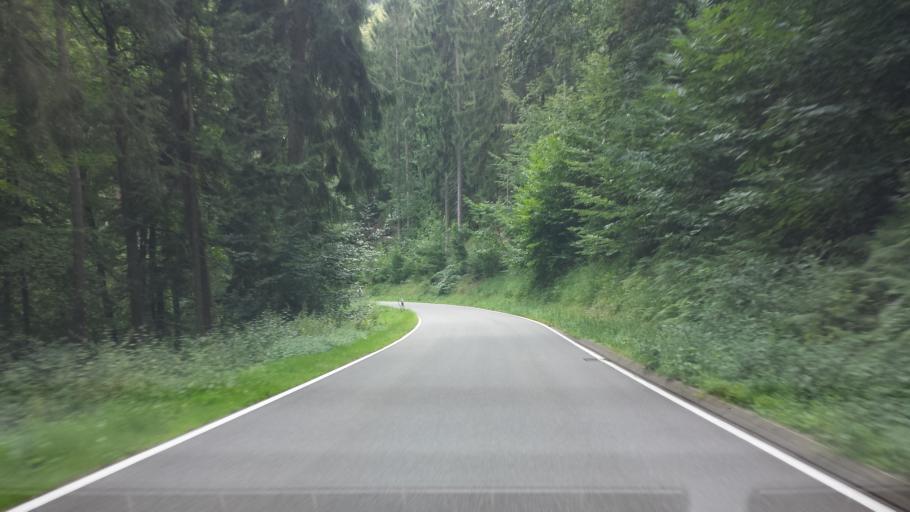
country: DE
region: Rheinland-Pfalz
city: Ramberg
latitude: 49.2690
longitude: 8.0285
